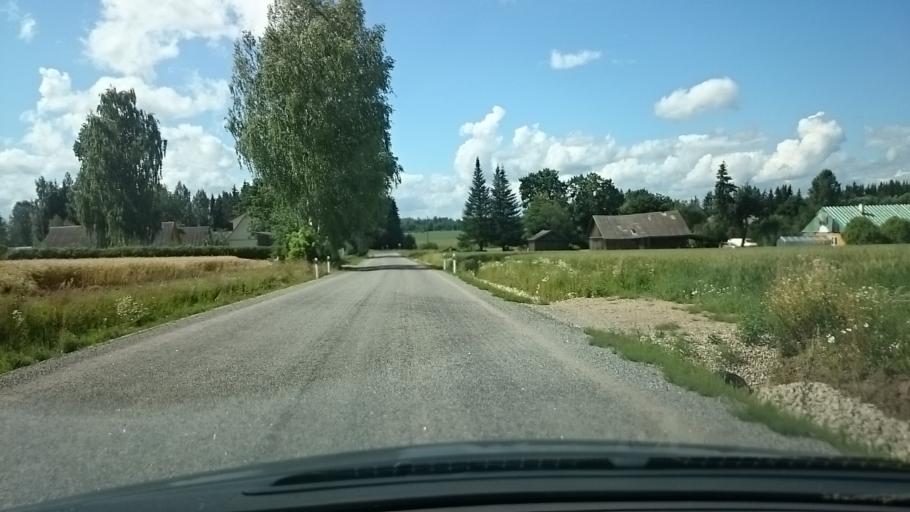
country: EE
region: Polvamaa
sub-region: Polva linn
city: Polva
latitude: 57.9681
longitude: 26.9648
